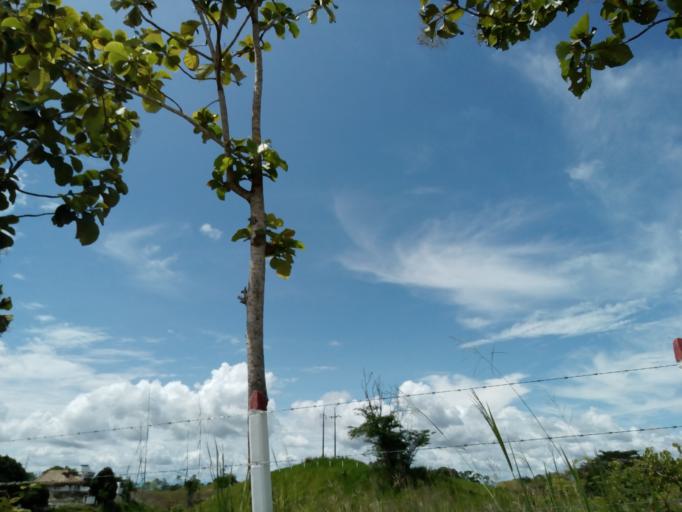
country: CO
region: Boyaca
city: Puerto Boyaca
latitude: 5.9659
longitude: -74.4410
